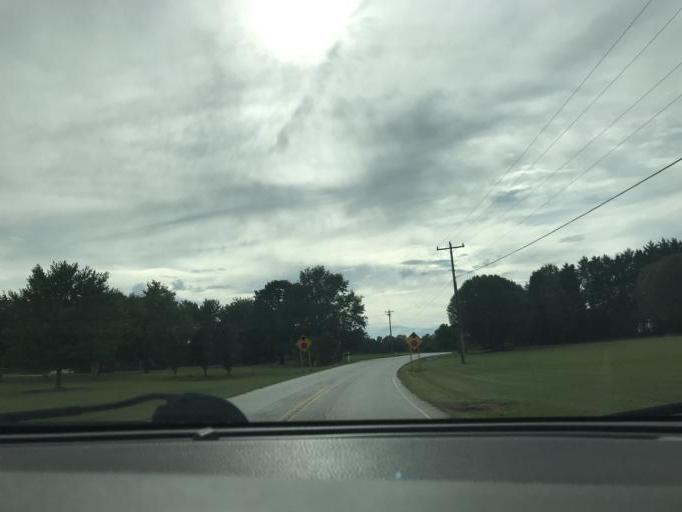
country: US
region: South Carolina
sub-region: Cherokee County
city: Gaffney
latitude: 35.1362
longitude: -81.6883
